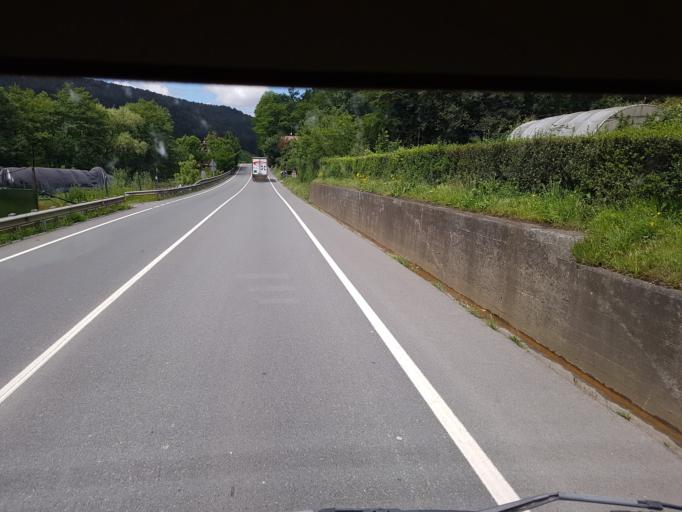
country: ES
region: Basque Country
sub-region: Bizkaia
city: Galdakao
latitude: 43.2306
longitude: -2.7834
